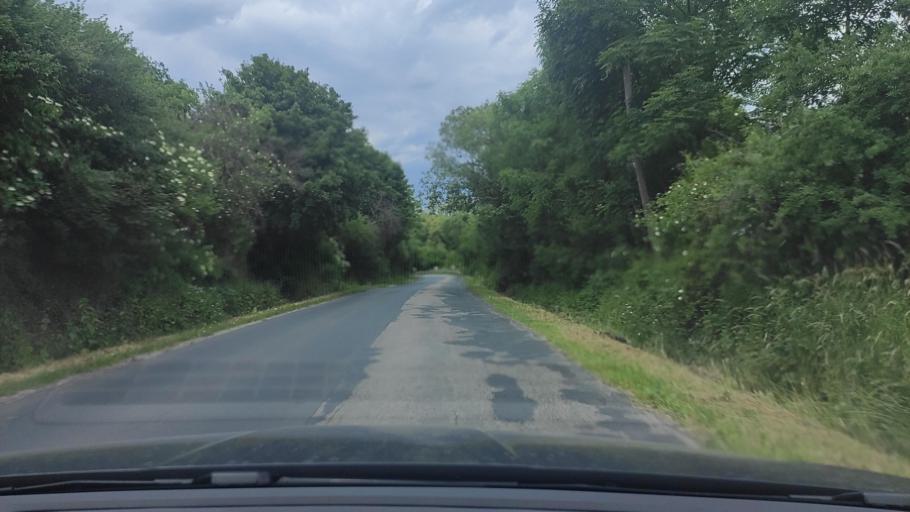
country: PL
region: Greater Poland Voivodeship
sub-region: Powiat poznanski
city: Kostrzyn
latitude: 52.4459
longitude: 17.1680
